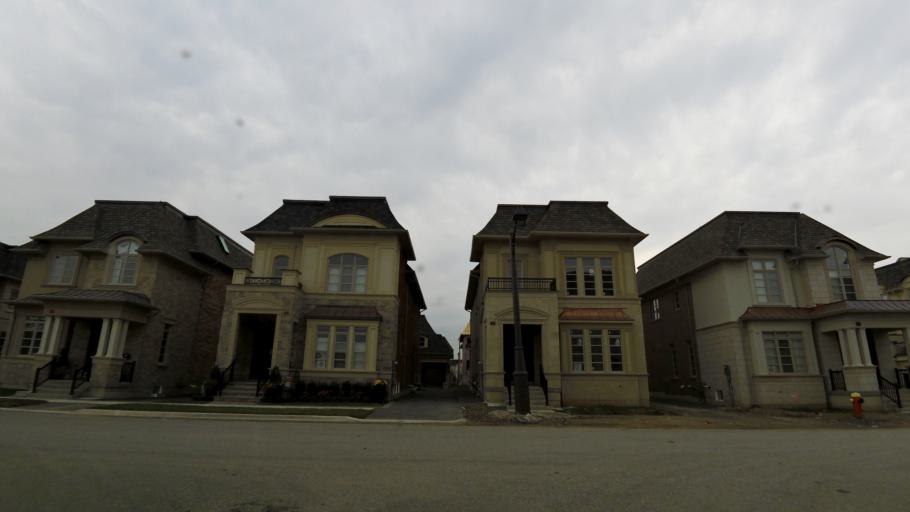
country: CA
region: Ontario
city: Oakville
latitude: 43.4373
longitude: -79.6839
